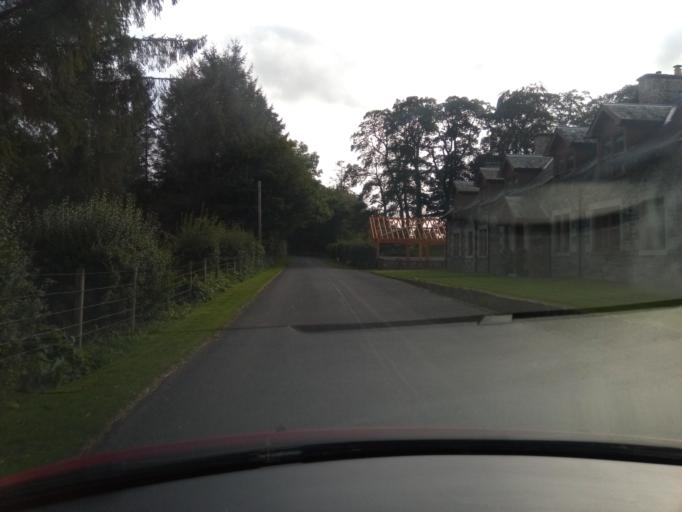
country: GB
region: Scotland
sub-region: The Scottish Borders
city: Kelso
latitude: 55.5000
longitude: -2.3475
